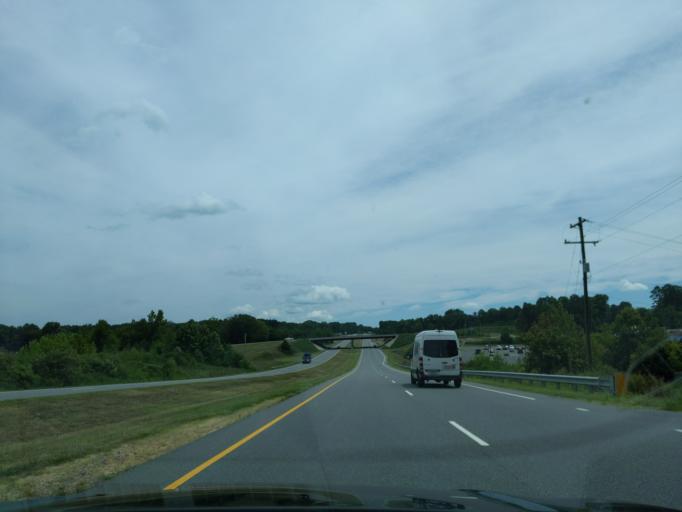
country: US
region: North Carolina
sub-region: Cabarrus County
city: Mount Pleasant
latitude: 35.4051
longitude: -80.4560
